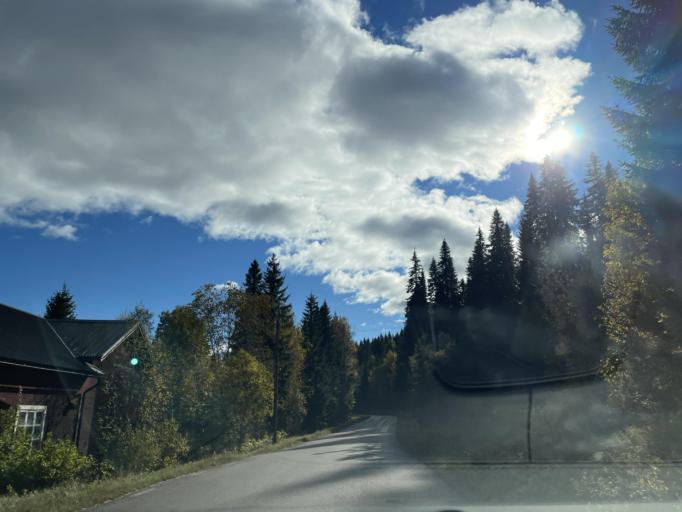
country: SE
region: Dalarna
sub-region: Malung-Saelens kommun
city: Malung
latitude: 61.1406
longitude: 13.2698
